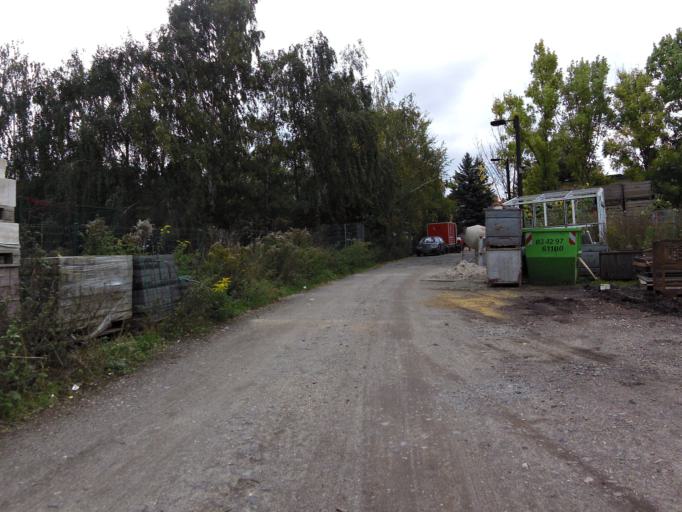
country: DE
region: Saxony
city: Grossposna
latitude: 51.3083
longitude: 12.4536
